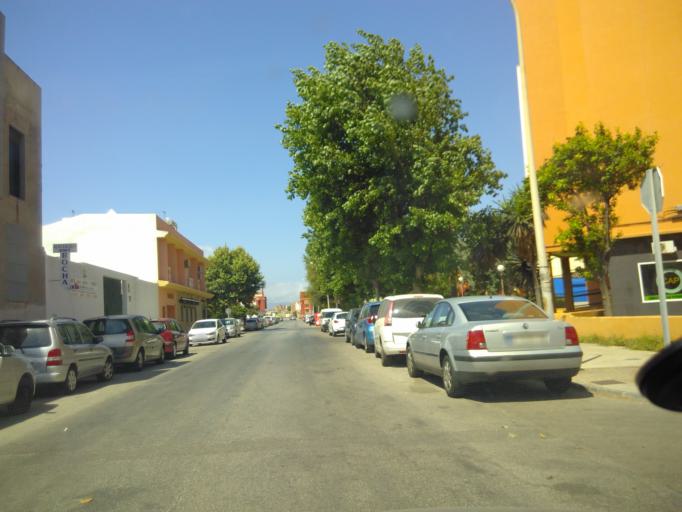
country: ES
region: Andalusia
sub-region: Provincia de Cadiz
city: La Linea de la Concepcion
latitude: 36.1707
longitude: -5.3495
